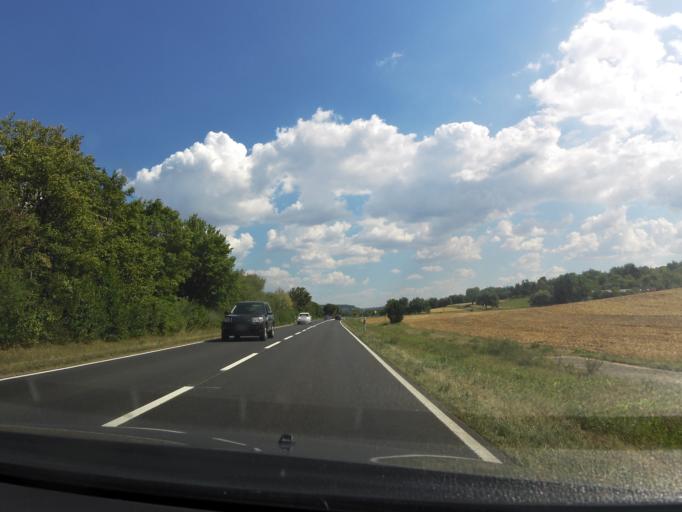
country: DE
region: Bavaria
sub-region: Regierungsbezirk Unterfranken
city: Erlabrunn
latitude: 49.8517
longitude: 9.8534
